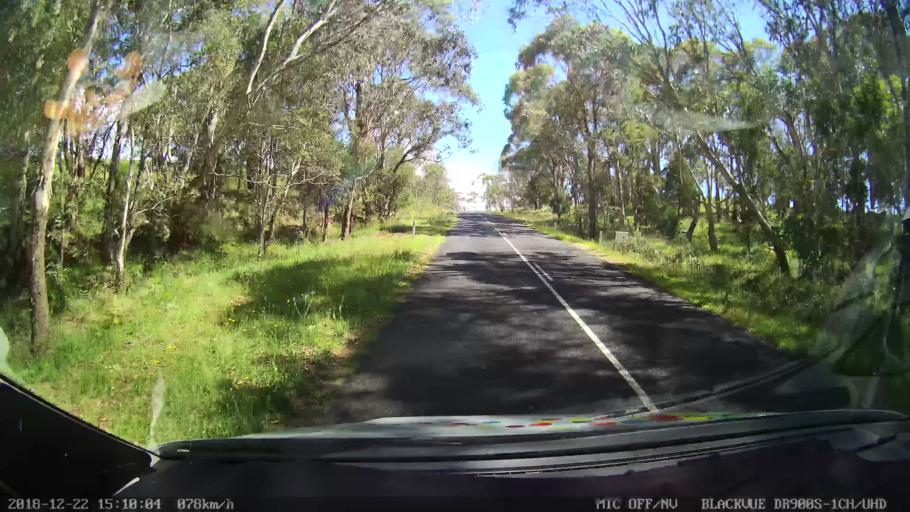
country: AU
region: New South Wales
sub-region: Bellingen
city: Dorrigo
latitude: -30.3309
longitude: 152.4055
